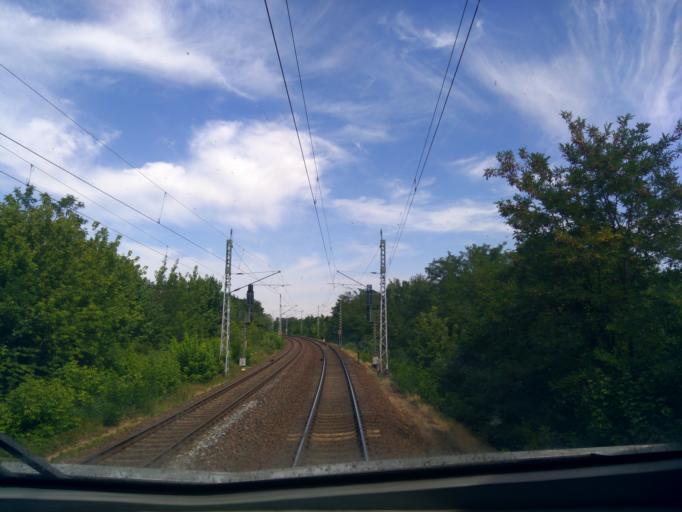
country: DE
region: Berlin
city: Adlershof
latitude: 52.4277
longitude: 13.5626
